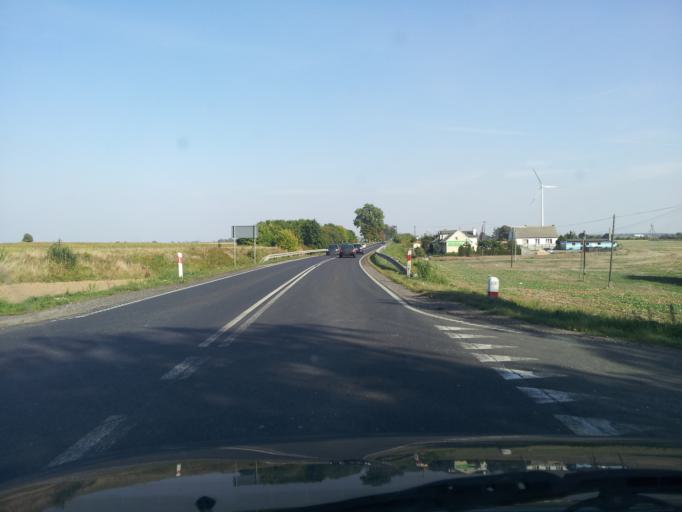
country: PL
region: Kujawsko-Pomorskie
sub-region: Powiat mogilenski
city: Strzelno
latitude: 52.6297
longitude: 18.1208
